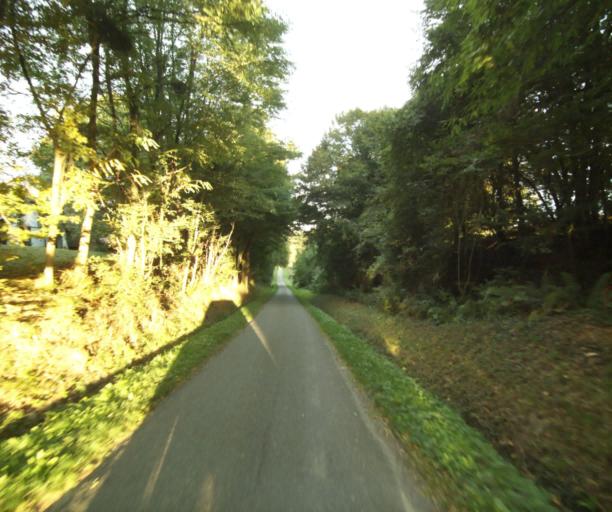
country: FR
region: Midi-Pyrenees
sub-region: Departement du Gers
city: Eauze
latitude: 43.8911
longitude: 0.0543
